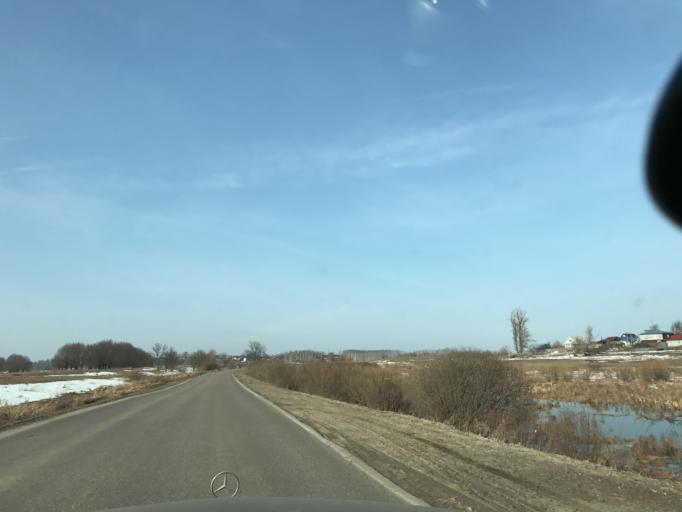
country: RU
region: Nizjnij Novgorod
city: Pavlovo
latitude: 55.9810
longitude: 43.0484
